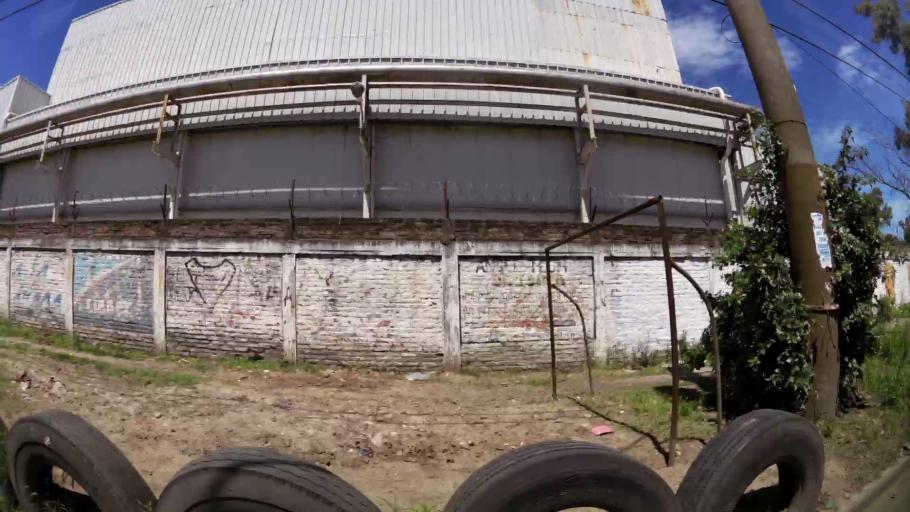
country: AR
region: Buenos Aires
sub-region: Partido de Quilmes
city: Quilmes
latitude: -34.7319
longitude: -58.3232
